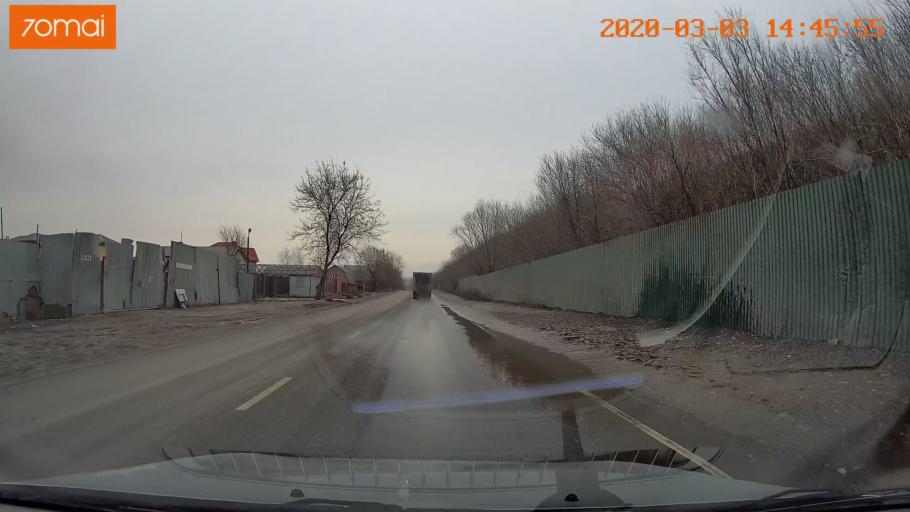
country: RU
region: Moskovskaya
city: Rodniki
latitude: 55.6984
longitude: 38.0533
